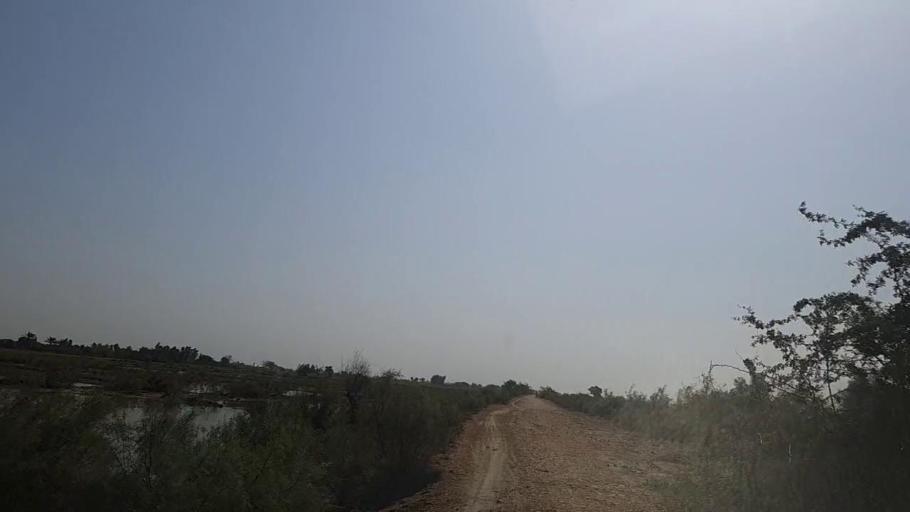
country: PK
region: Sindh
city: Daro Mehar
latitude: 24.7129
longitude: 68.1211
